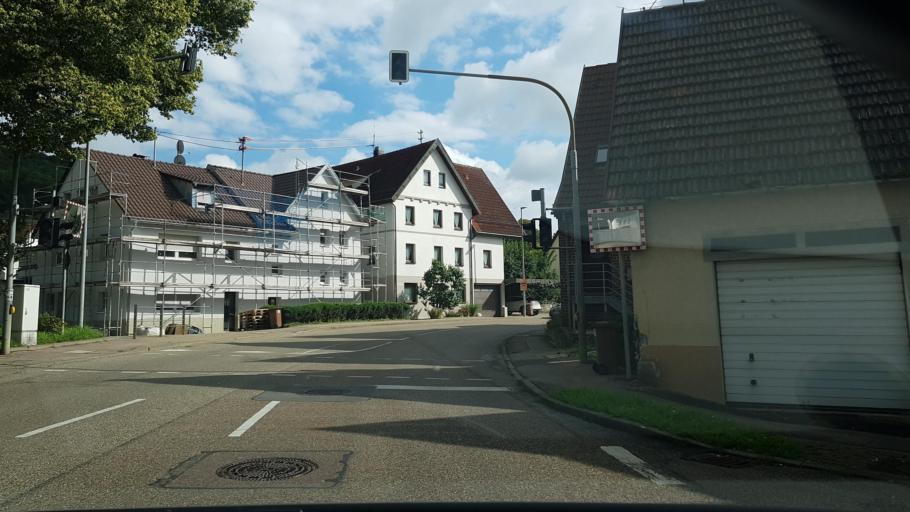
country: DE
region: Baden-Wuerttemberg
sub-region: Regierungsbezirk Stuttgart
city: Owen
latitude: 48.5760
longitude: 9.4564
